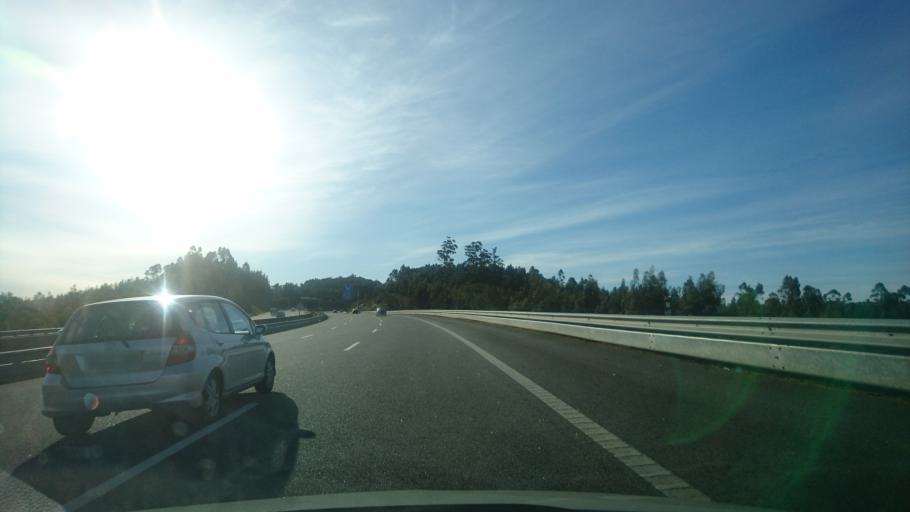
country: PT
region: Porto
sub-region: Vila Nova de Gaia
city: Sandim
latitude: 41.0300
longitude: -8.4881
